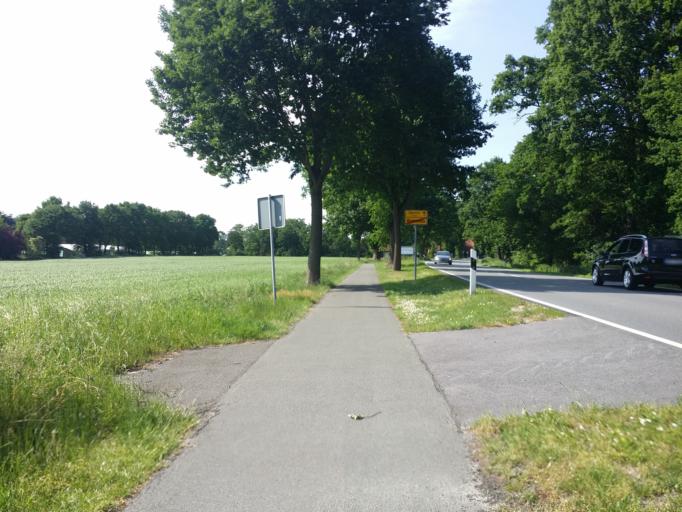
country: DE
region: Lower Saxony
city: Wiefelstede
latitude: 53.2622
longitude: 8.1128
